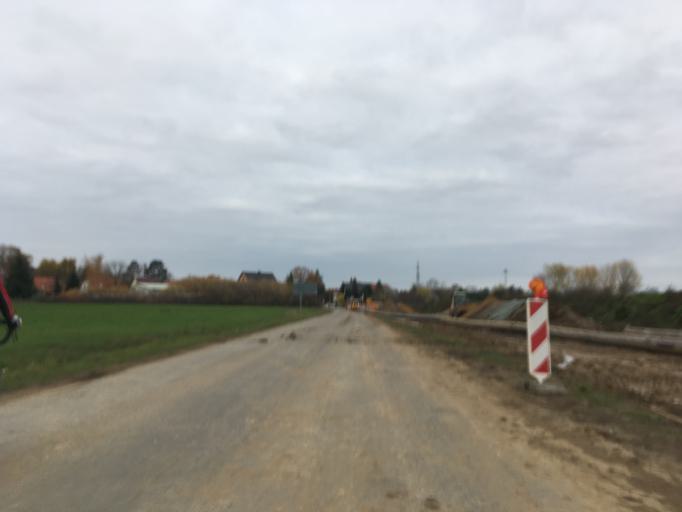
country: DE
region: Brandenburg
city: Frankfurt (Oder)
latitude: 52.3077
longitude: 14.5294
